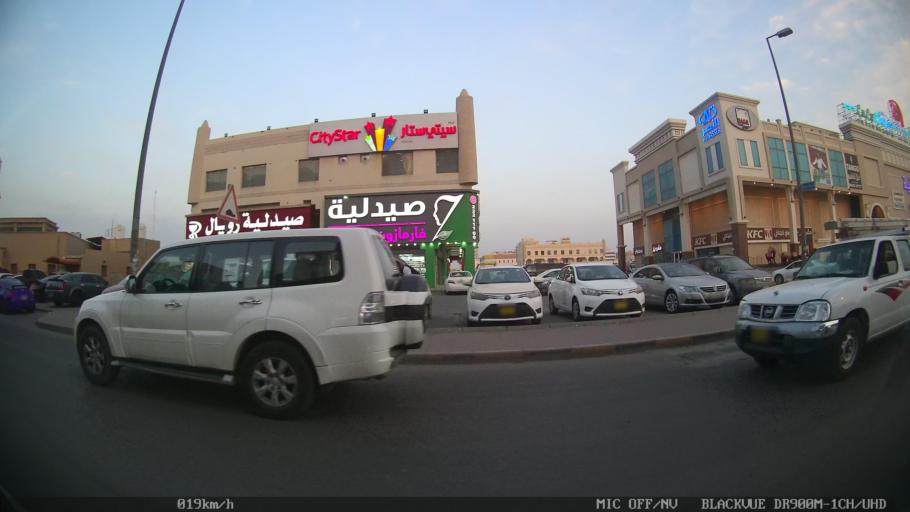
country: KW
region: Al Farwaniyah
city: Al Farwaniyah
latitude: 29.2904
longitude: 47.9698
